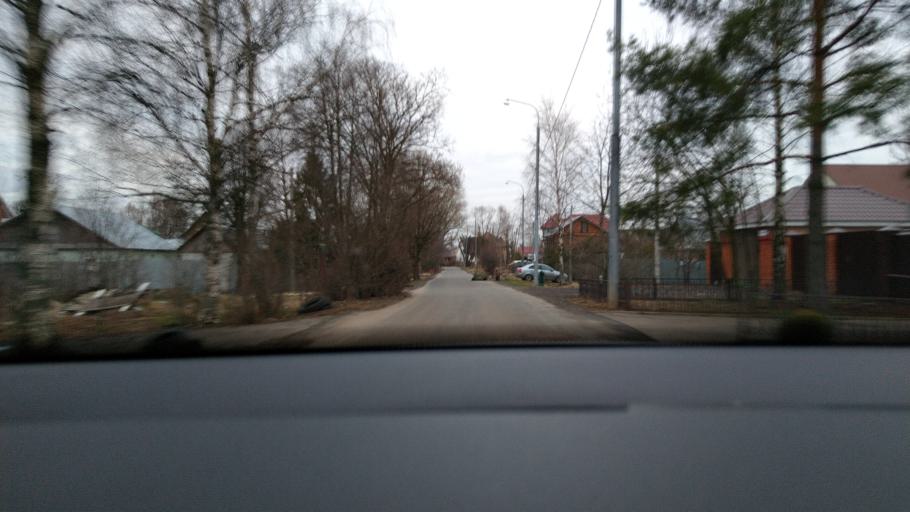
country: RU
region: Moscow
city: Vnukovo
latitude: 55.6059
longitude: 37.2118
